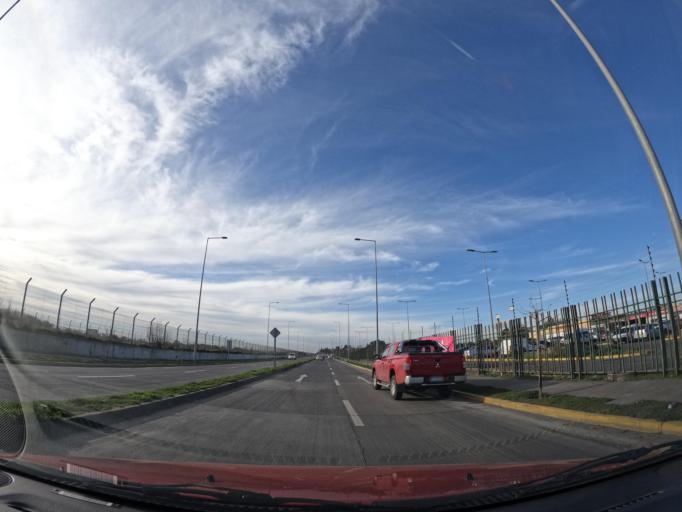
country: CL
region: Biobio
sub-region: Provincia de Concepcion
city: Concepcion
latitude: -36.7901
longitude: -73.0693
